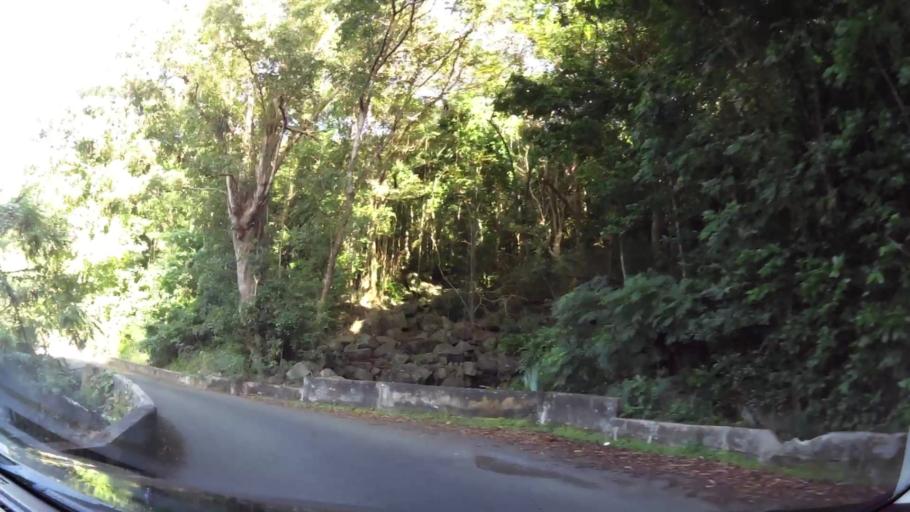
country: VG
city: Road Town
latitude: 18.4174
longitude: -64.6632
